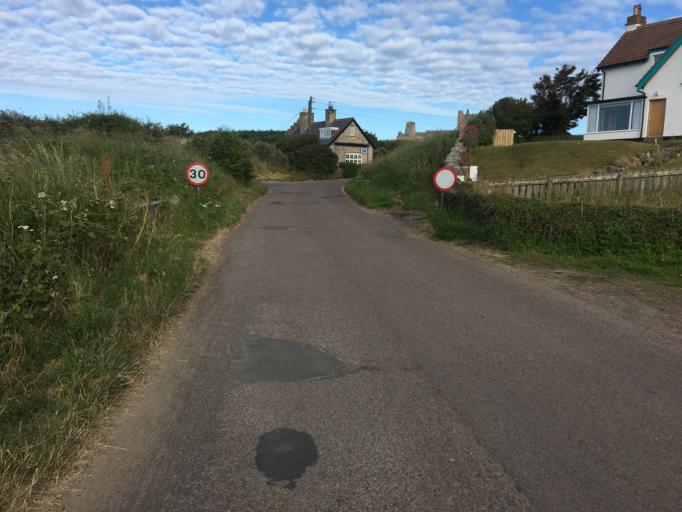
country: GB
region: England
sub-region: Northumberland
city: Bamburgh
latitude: 55.6113
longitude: -1.7179
